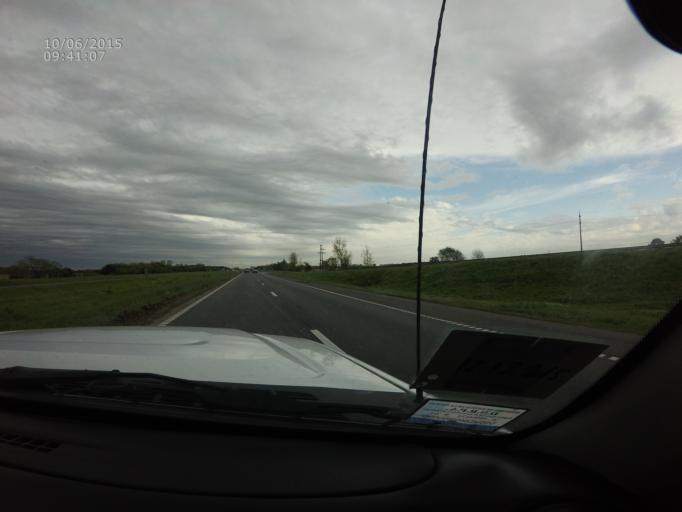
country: AR
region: Buenos Aires
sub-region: Partido de Zarate
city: Zarate
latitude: -34.0800
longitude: -59.2108
